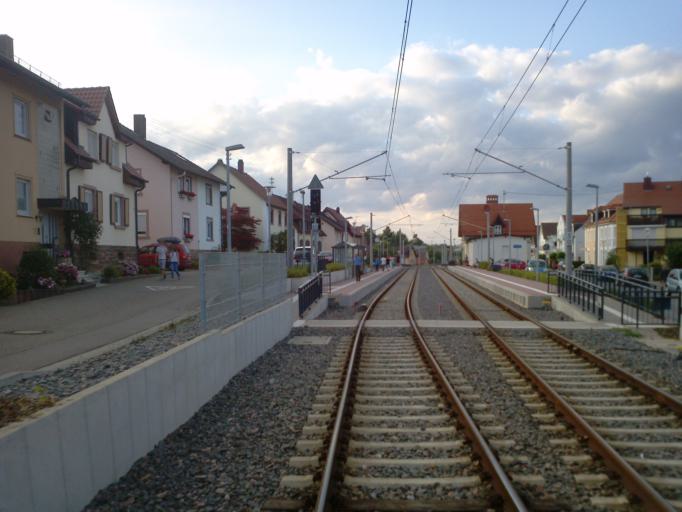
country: DE
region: Baden-Wuerttemberg
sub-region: Karlsruhe Region
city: Ettlingen
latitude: 48.9146
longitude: 8.5032
